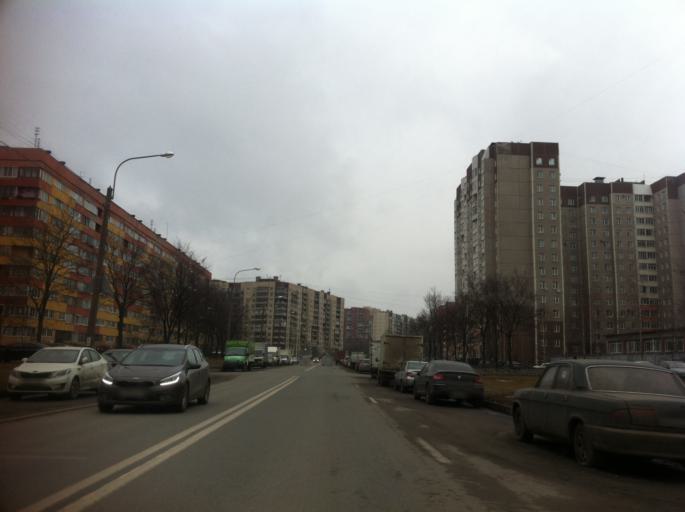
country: RU
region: St.-Petersburg
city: Uritsk
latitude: 59.8530
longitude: 30.1853
